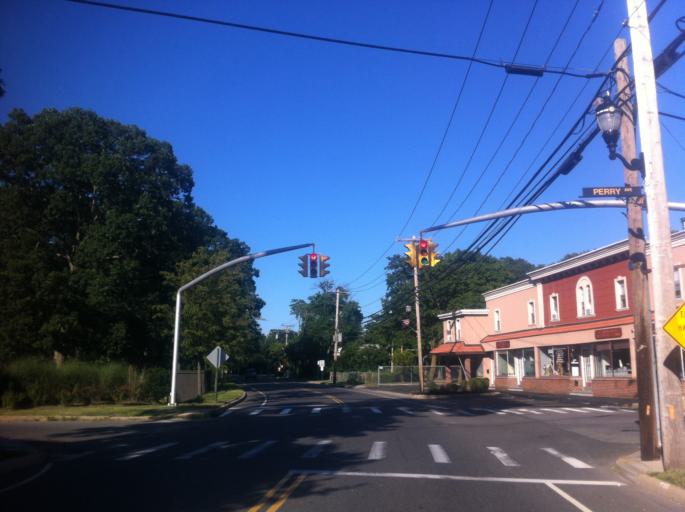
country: US
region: New York
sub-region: Nassau County
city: Bayville
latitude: 40.9110
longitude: -73.5739
